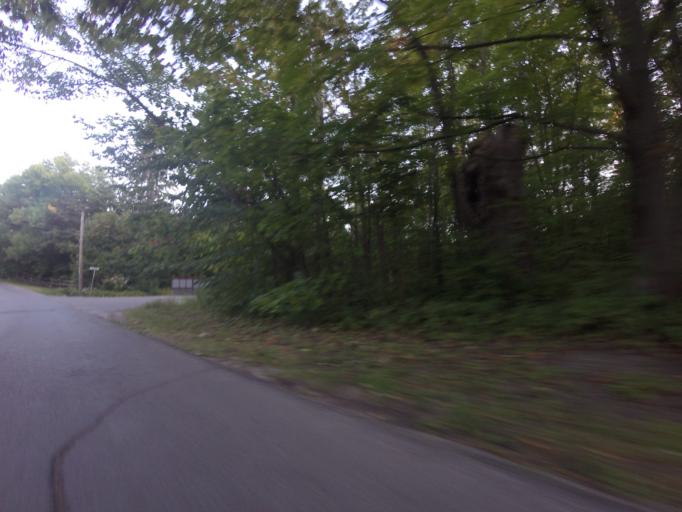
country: CA
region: Quebec
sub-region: Laurentides
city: Oka
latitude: 45.4523
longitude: -74.1162
